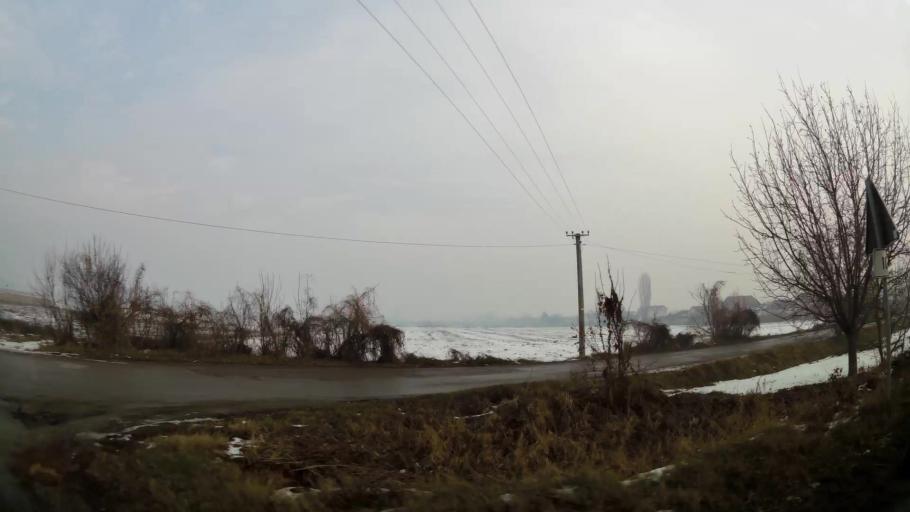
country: MK
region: Ilinden
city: Jurumleri
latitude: 41.9771
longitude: 21.5335
